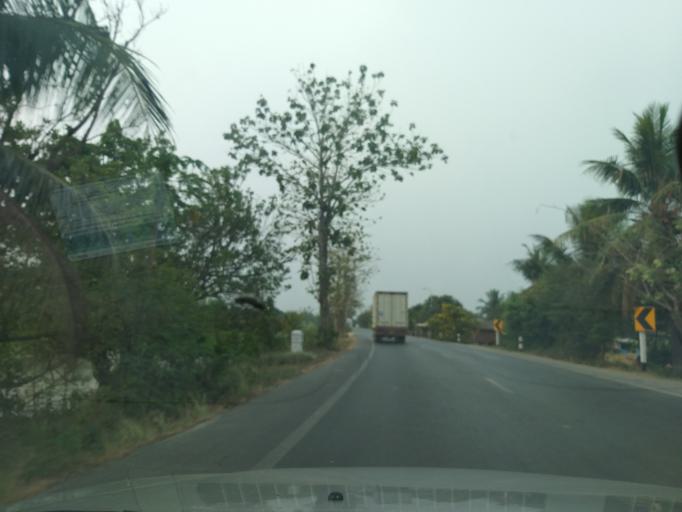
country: TH
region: Bangkok
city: Nong Chok
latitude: 13.9425
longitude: 100.8950
